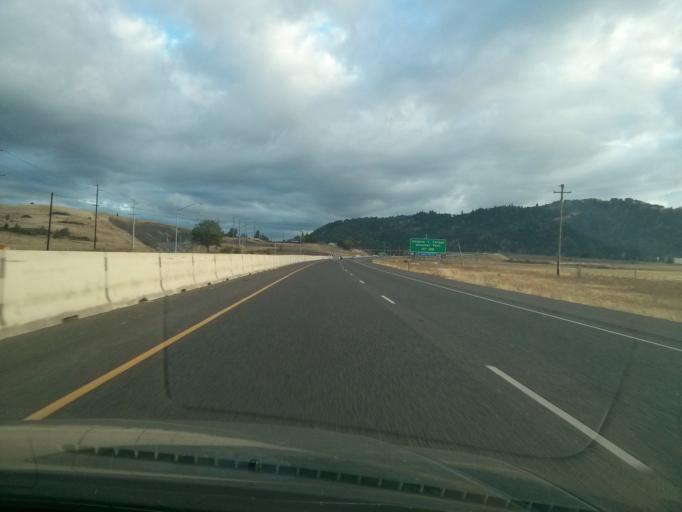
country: US
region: Oregon
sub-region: Douglas County
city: Roseburg North
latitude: 43.2983
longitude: -123.3505
